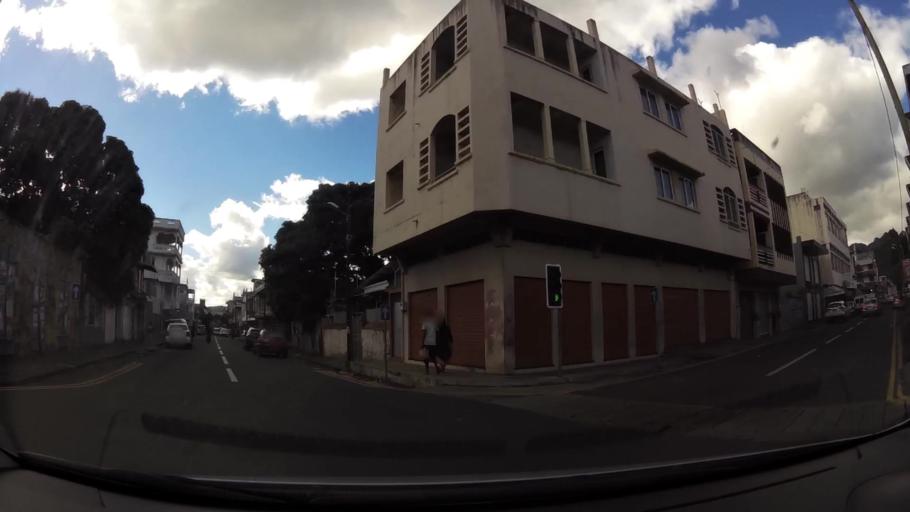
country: MU
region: Port Louis
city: Port Louis
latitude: -20.1582
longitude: 57.5109
